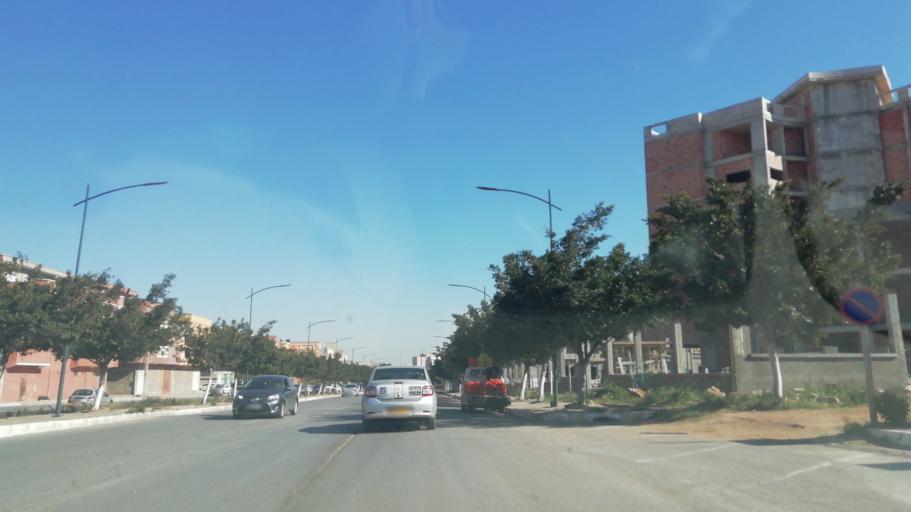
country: DZ
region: Oran
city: Bir el Djir
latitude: 35.7166
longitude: -0.5908
